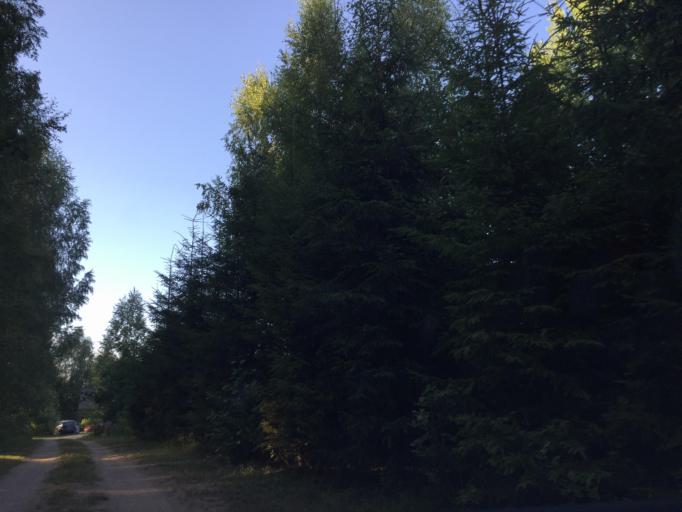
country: LV
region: Talsu Rajons
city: Stende
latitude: 57.1617
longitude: 22.3041
